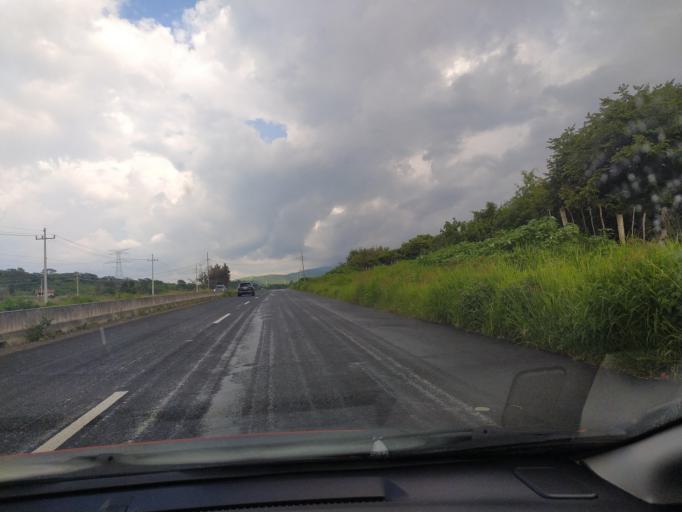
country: MX
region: Jalisco
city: Bellavista
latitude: 20.4335
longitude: -103.5960
